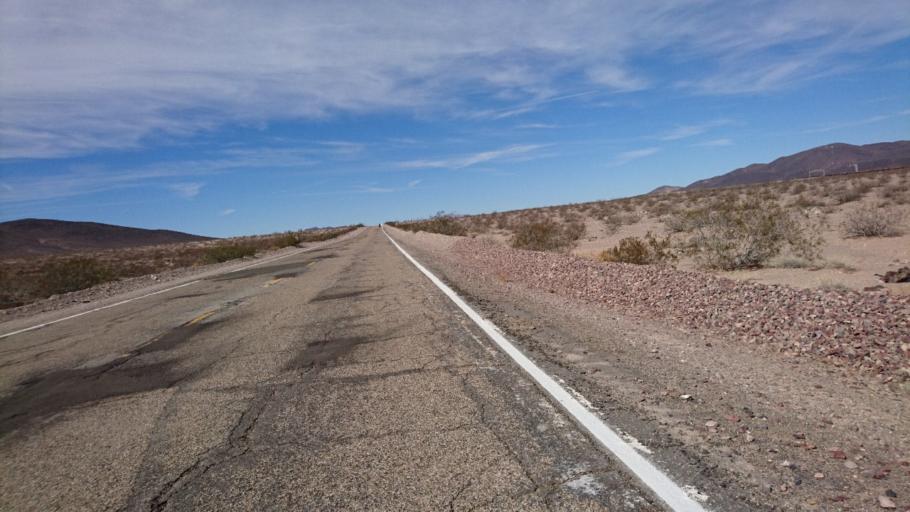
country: US
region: California
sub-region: San Bernardino County
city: Twentynine Palms
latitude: 34.6932
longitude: -116.0496
